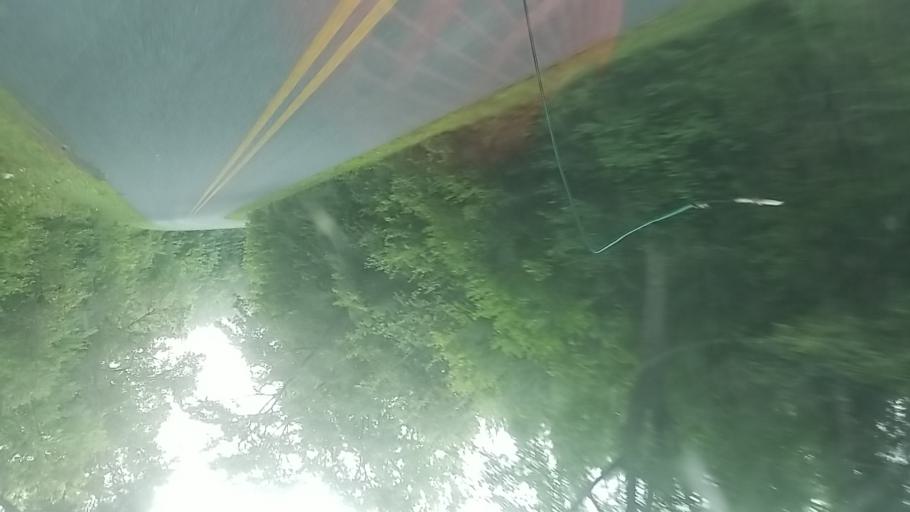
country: US
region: Maryland
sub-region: Wicomico County
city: Pittsville
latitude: 38.4140
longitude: -75.4852
